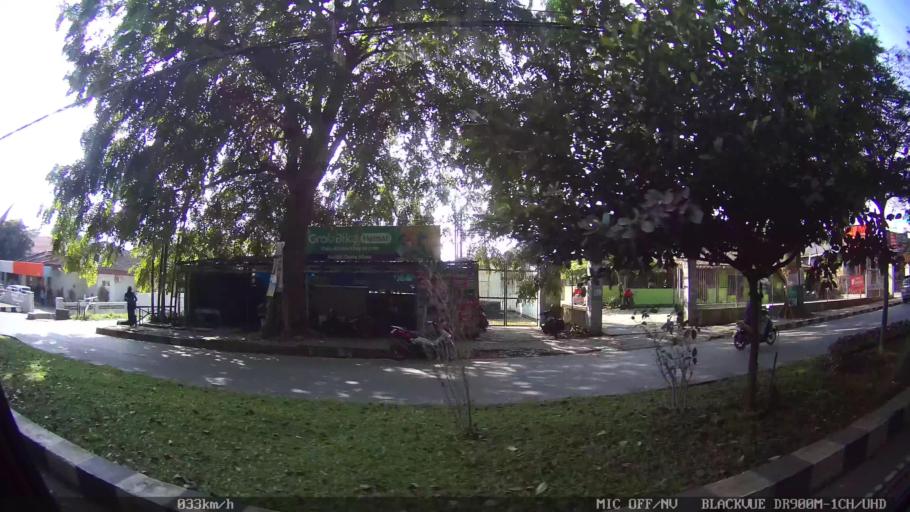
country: ID
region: Lampung
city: Kedaton
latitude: -5.3695
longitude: 105.2413
